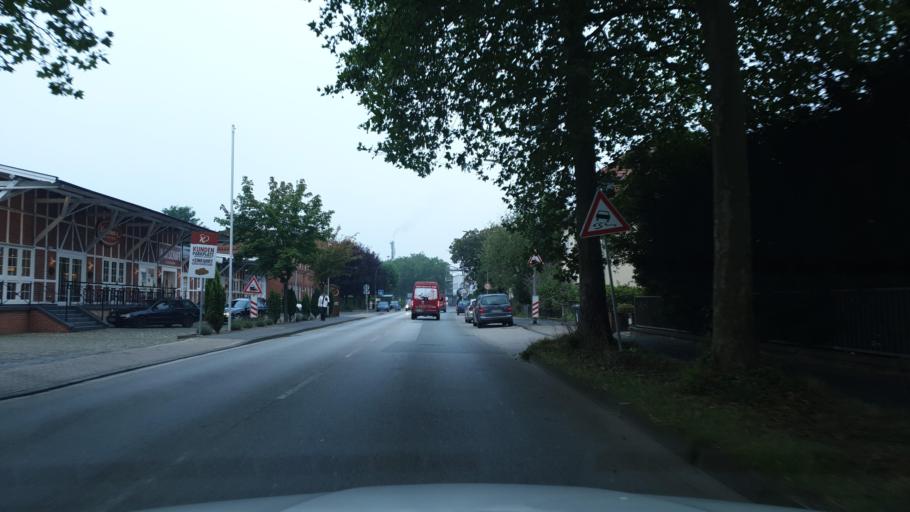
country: DE
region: North Rhine-Westphalia
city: Bad Oeynhausen
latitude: 52.1973
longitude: 8.8055
